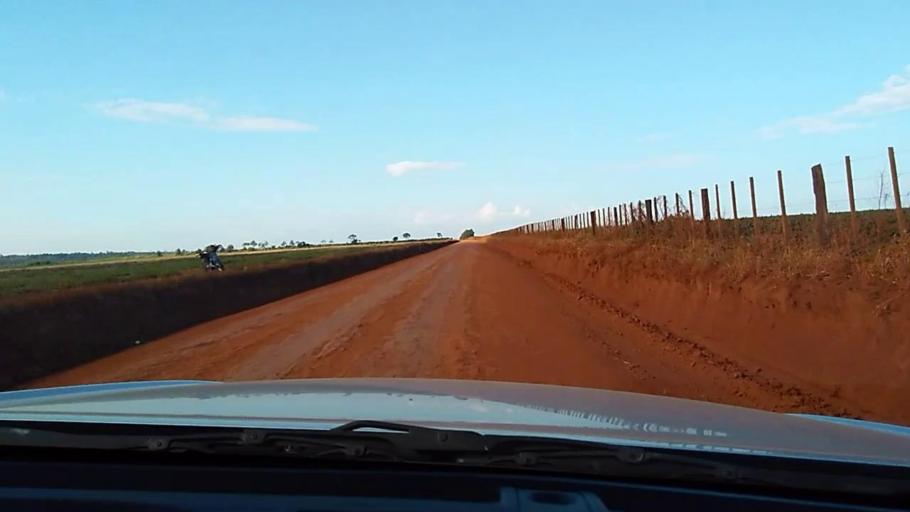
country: PY
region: Alto Parana
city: Naranjal
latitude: -25.7091
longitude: -55.3903
